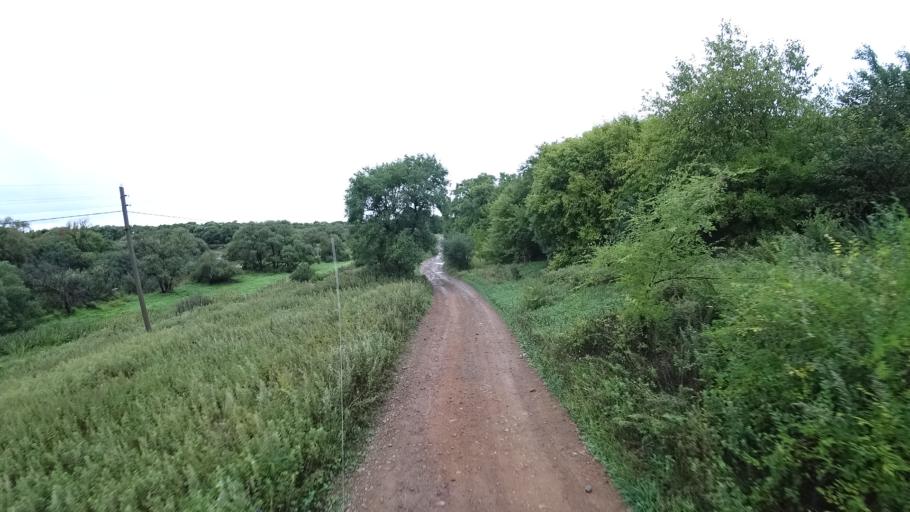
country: RU
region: Primorskiy
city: Monastyrishche
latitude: 44.2688
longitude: 132.4040
